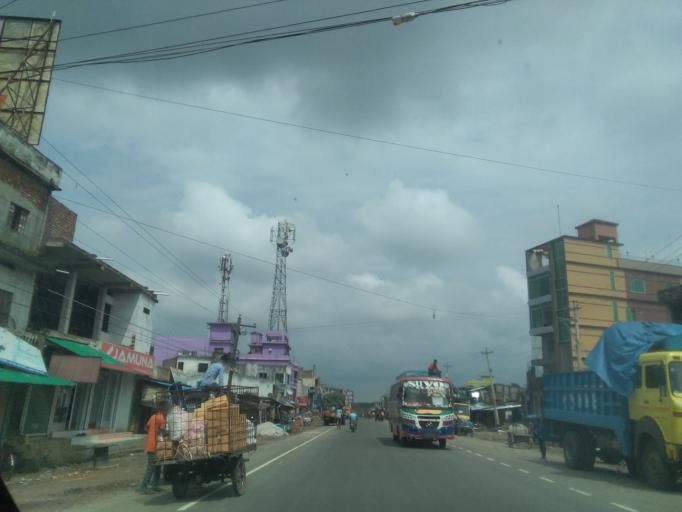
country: BD
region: Khulna
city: Kesabpur
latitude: 22.8398
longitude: 89.2975
